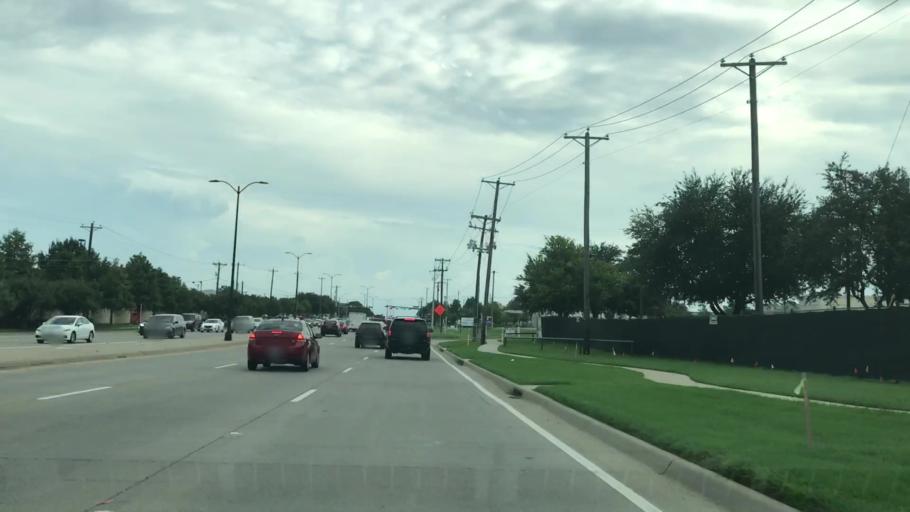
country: US
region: Texas
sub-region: Collin County
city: Frisco
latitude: 33.1246
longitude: -96.8057
